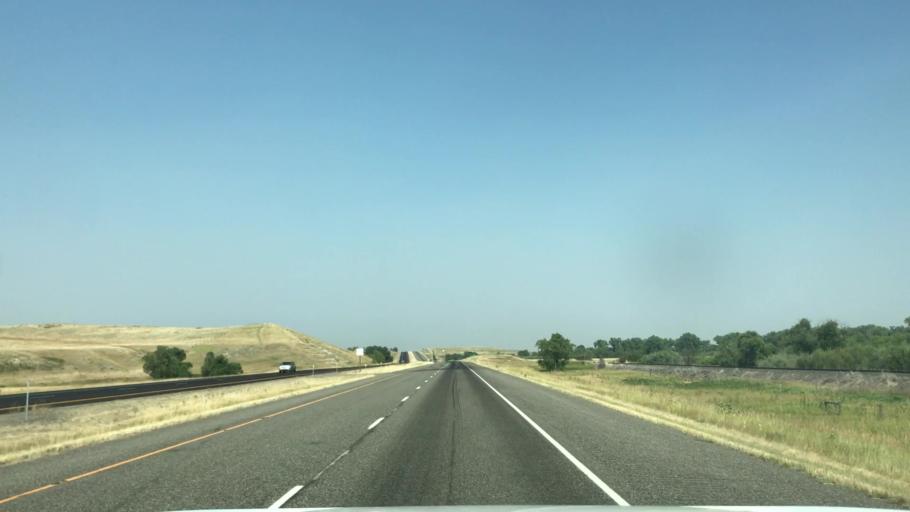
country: US
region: Montana
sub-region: Cascade County
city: Sun Prairie
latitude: 47.2385
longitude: -111.7354
